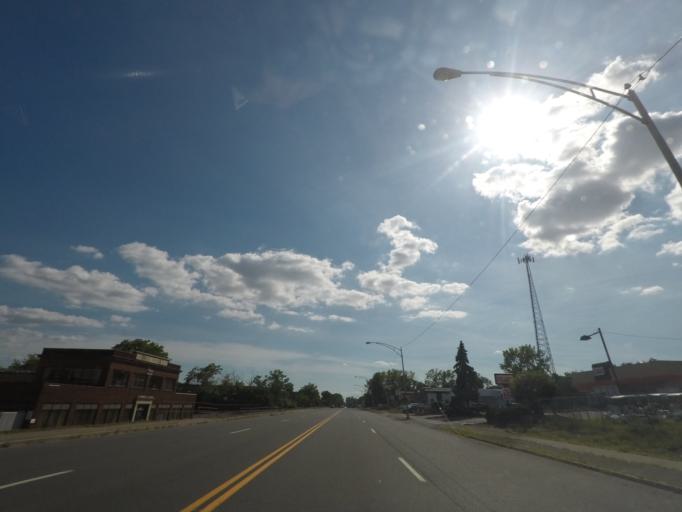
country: US
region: New York
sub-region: Albany County
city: Menands
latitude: 42.6805
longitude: -73.7329
